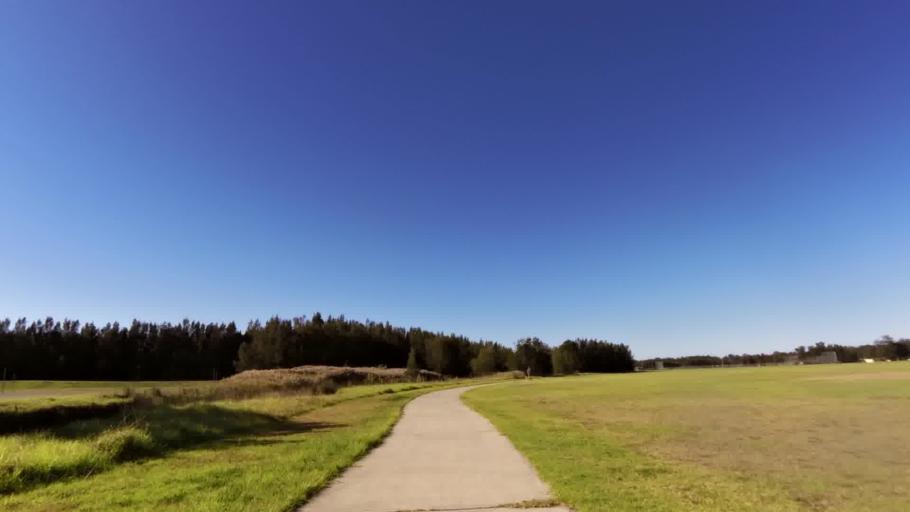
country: AU
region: New South Wales
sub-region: Wollongong
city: Berkeley
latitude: -34.4803
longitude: 150.8348
